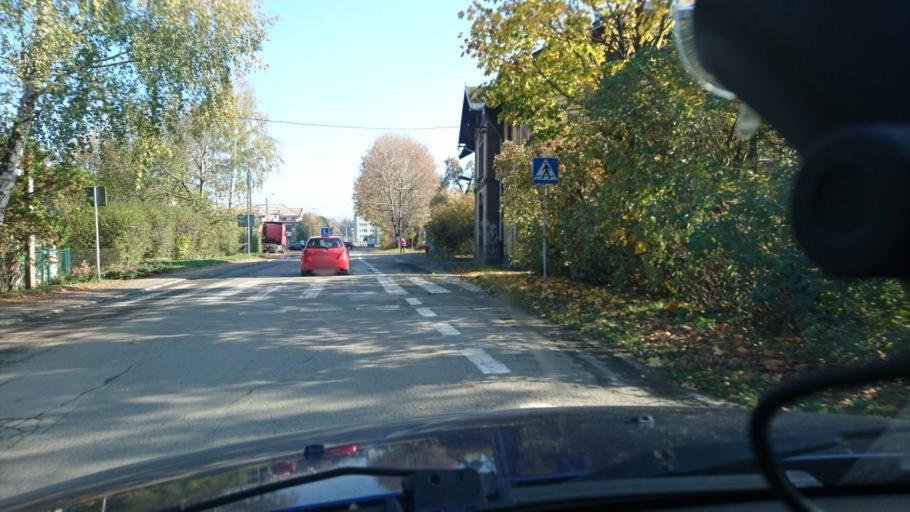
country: PL
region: Silesian Voivodeship
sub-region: Powiat bielski
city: Jaworze
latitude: 49.8113
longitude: 18.9803
